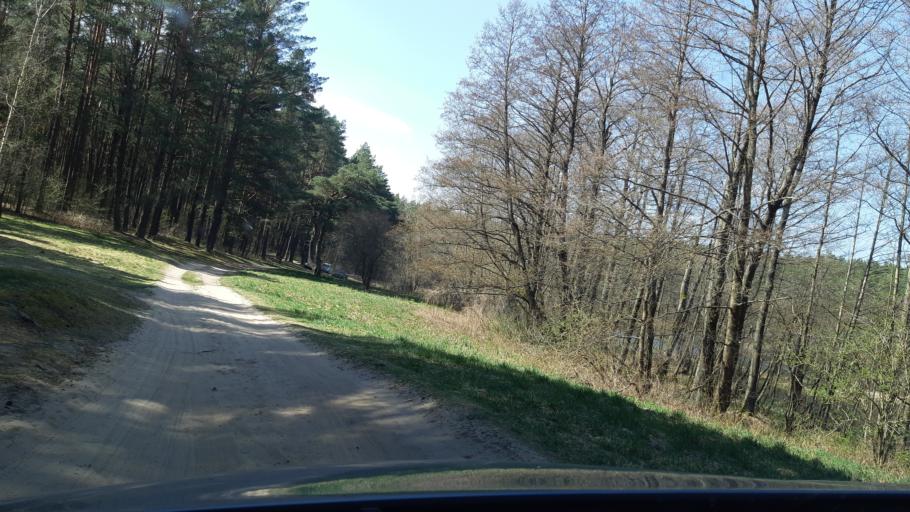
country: LT
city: Virbalis
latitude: 54.5693
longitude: 22.9036
